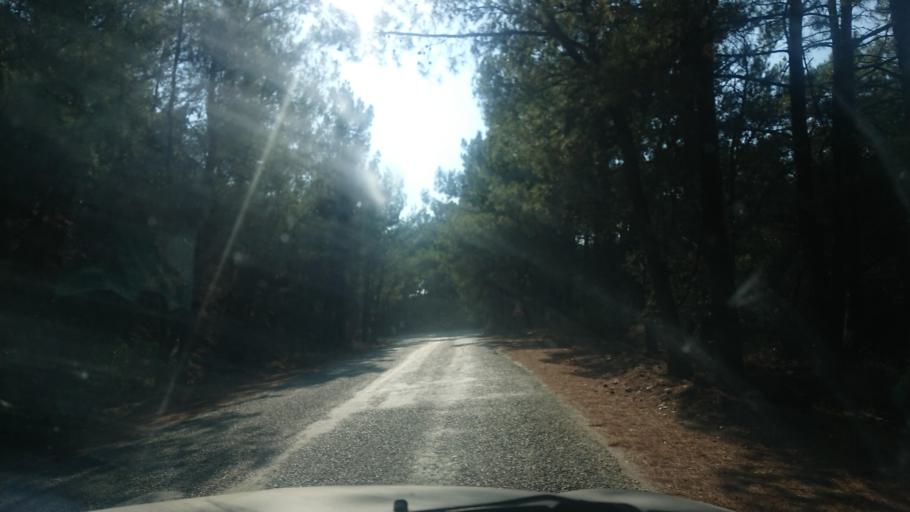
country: TR
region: Aydin
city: Atburgazi
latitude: 37.6887
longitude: 27.1255
